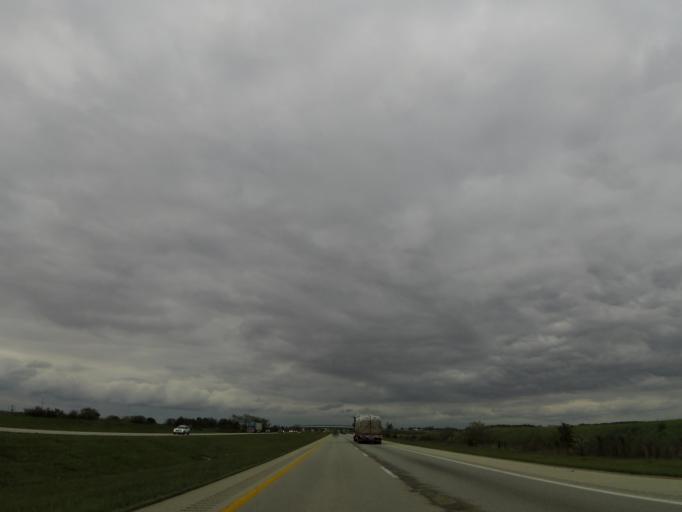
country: US
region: Ohio
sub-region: Greene County
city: Shawnee Hills
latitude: 39.5450
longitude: -83.7551
